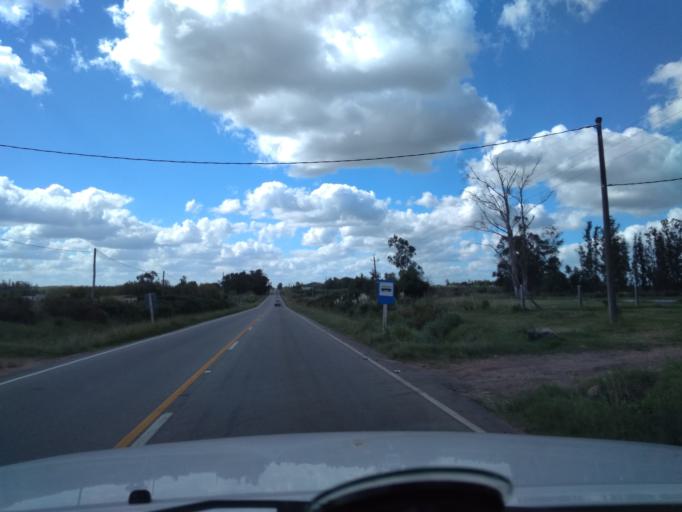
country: UY
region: Canelones
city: Joaquin Suarez
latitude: -34.7005
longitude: -56.0570
